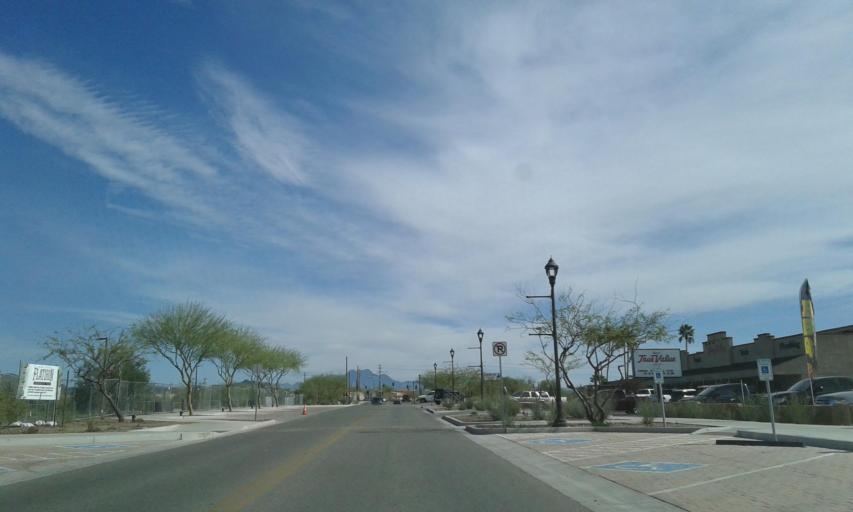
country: US
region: Arizona
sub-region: Pinal County
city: Apache Junction
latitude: 33.4167
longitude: -111.5483
